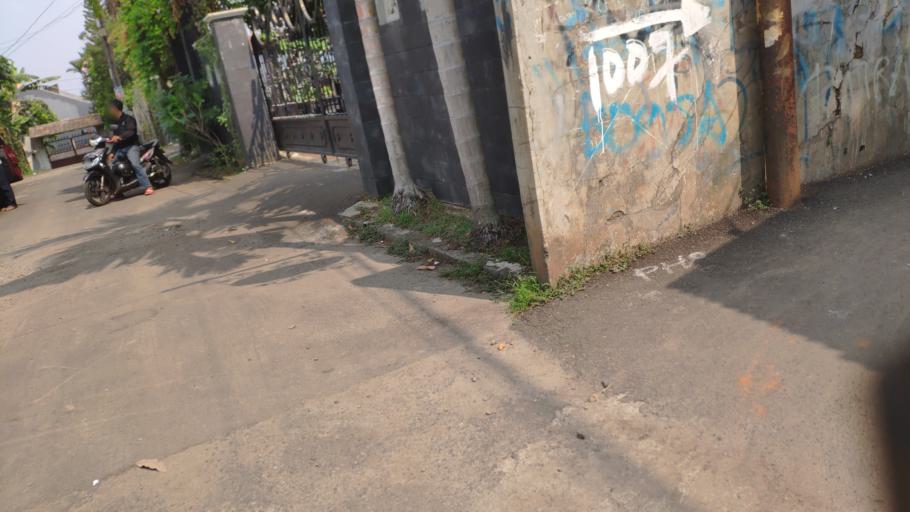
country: ID
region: West Java
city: Depok
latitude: -6.3072
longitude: 106.8285
